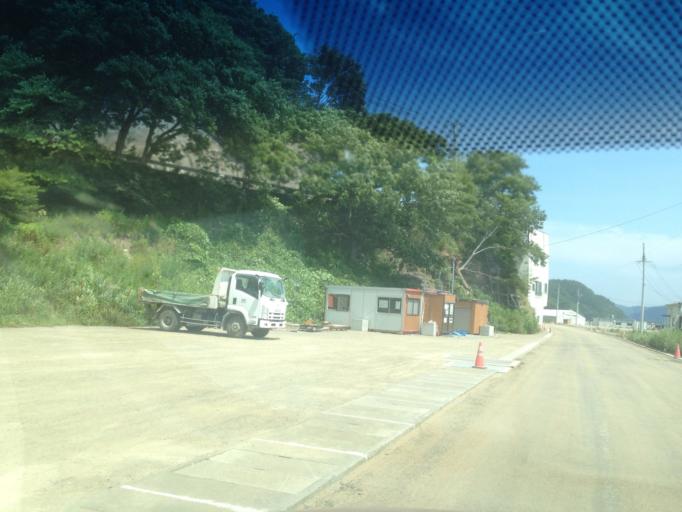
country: JP
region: Iwate
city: Otsuchi
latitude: 39.3541
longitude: 141.9257
